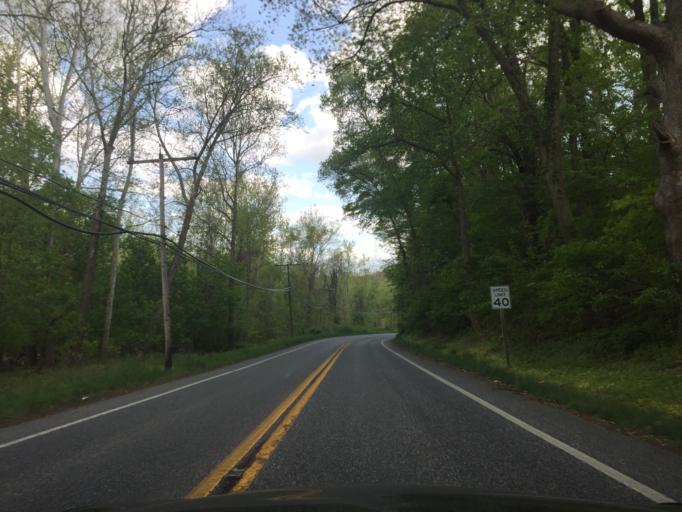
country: US
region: Maryland
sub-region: Baltimore County
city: Mays Chapel
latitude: 39.3903
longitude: -76.6603
